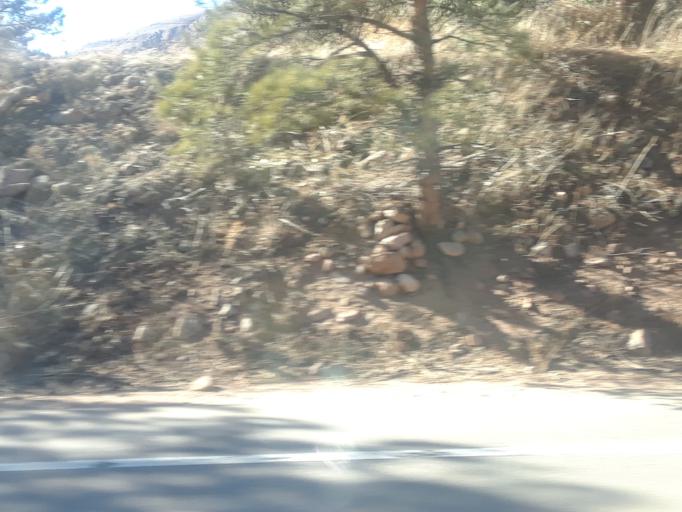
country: US
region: Colorado
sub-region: Boulder County
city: Lyons
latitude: 40.1252
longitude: -105.3048
